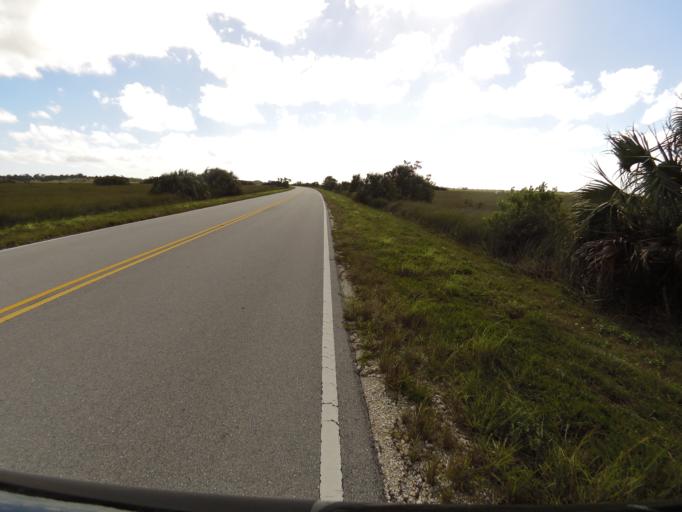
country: US
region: Florida
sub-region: Miami-Dade County
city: Florida City
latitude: 25.3595
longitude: -80.8211
